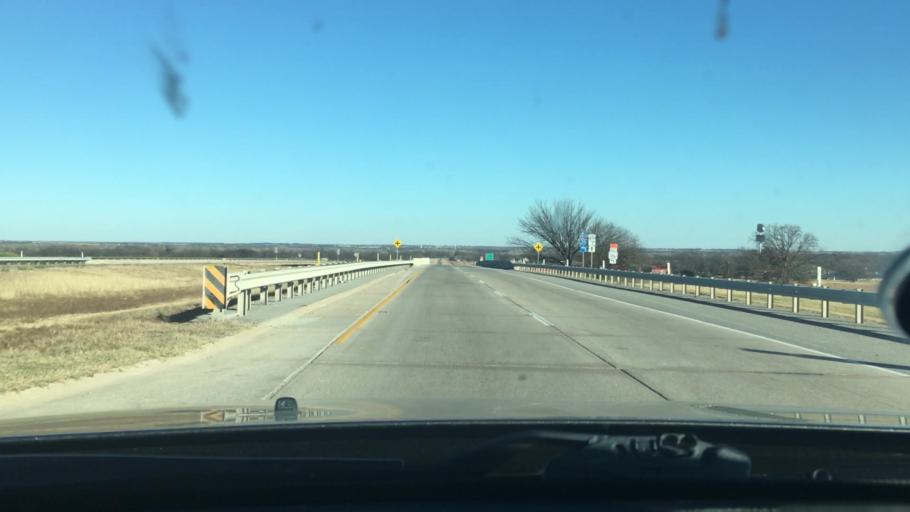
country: US
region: Oklahoma
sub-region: Murray County
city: Davis
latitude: 34.5064
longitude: -97.1760
